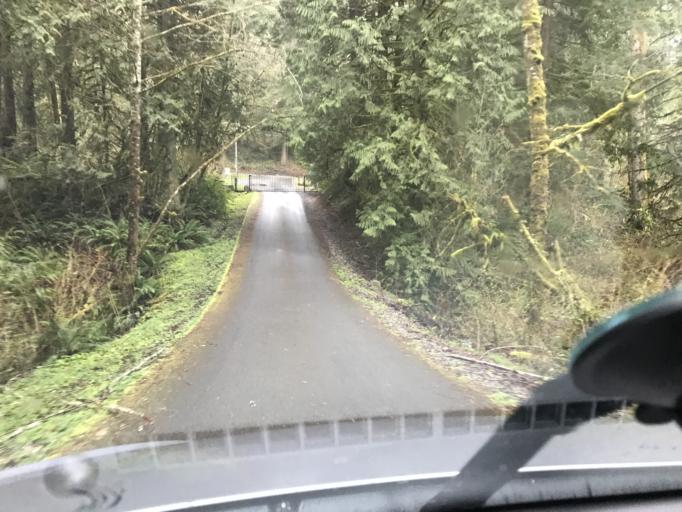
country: US
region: Washington
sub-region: King County
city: Ames Lake
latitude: 47.6496
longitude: -121.9601
